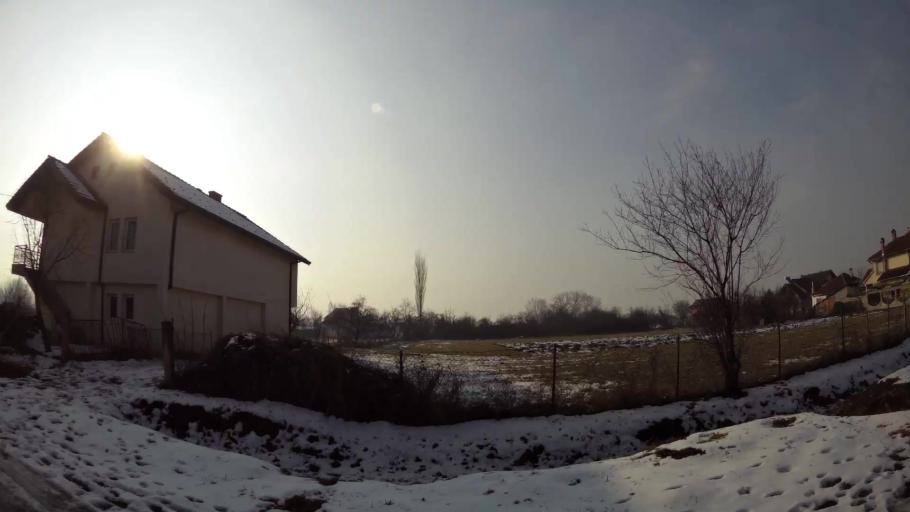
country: MK
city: Kadino
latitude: 41.9711
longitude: 21.5932
